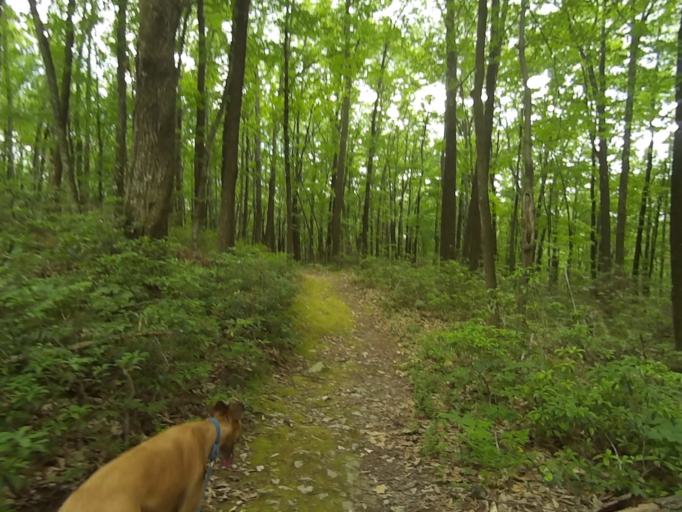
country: US
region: Pennsylvania
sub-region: Centre County
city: Stormstown
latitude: 40.9186
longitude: -78.0576
